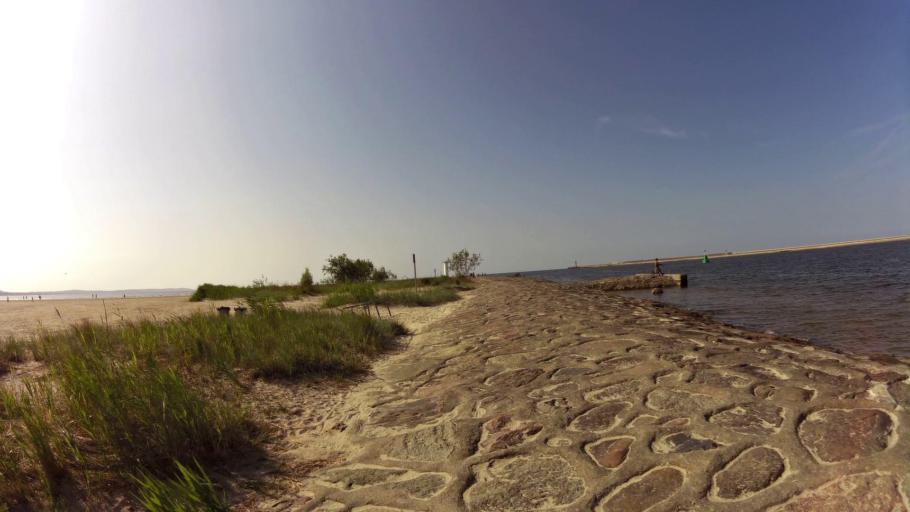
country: PL
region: West Pomeranian Voivodeship
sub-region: Swinoujscie
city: Swinoujscie
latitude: 53.9236
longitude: 14.2792
